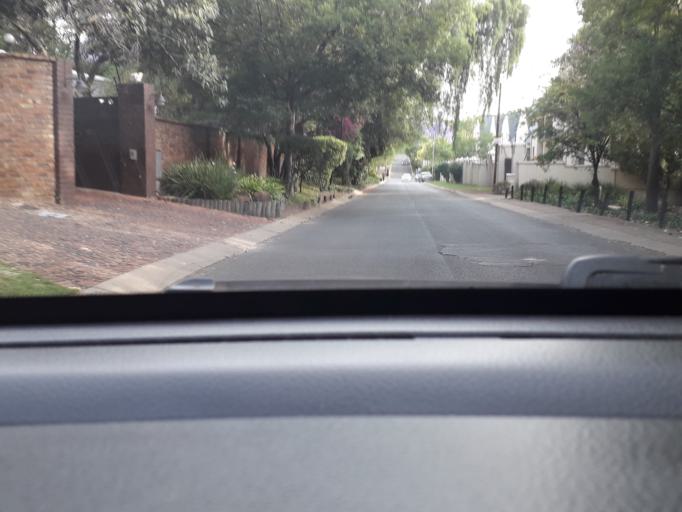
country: ZA
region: Gauteng
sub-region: City of Johannesburg Metropolitan Municipality
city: Midrand
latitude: -26.0501
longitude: 28.0556
